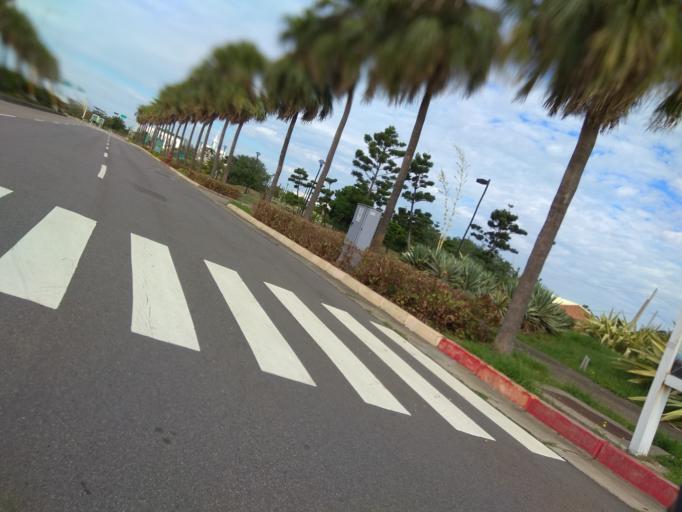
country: TW
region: Taiwan
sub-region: Hsinchu
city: Zhubei
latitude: 25.0336
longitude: 121.0723
